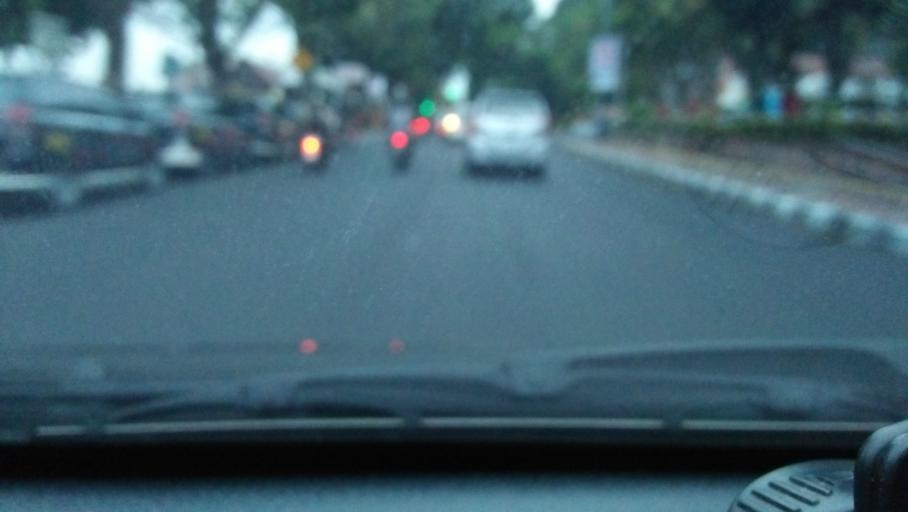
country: ID
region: Central Java
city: Magelang
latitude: -7.4923
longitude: 110.2226
